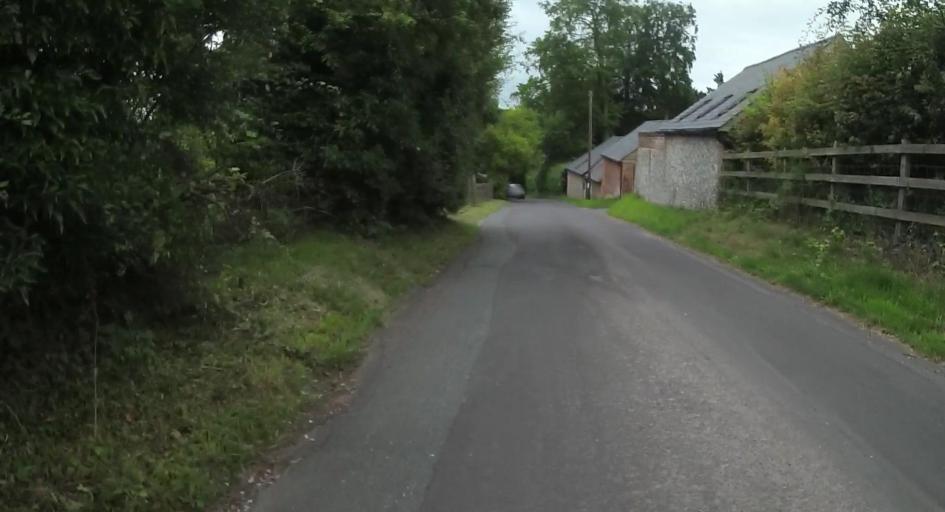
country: GB
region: England
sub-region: Hampshire
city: Kings Worthy
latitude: 51.0951
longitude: -1.2272
